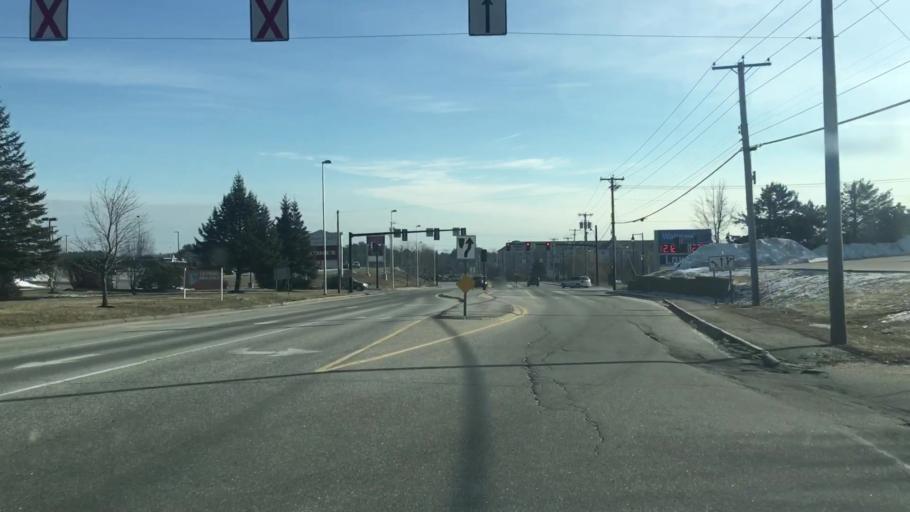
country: US
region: Maine
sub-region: Androscoggin County
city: Auburn
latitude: 44.1211
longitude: -70.2377
